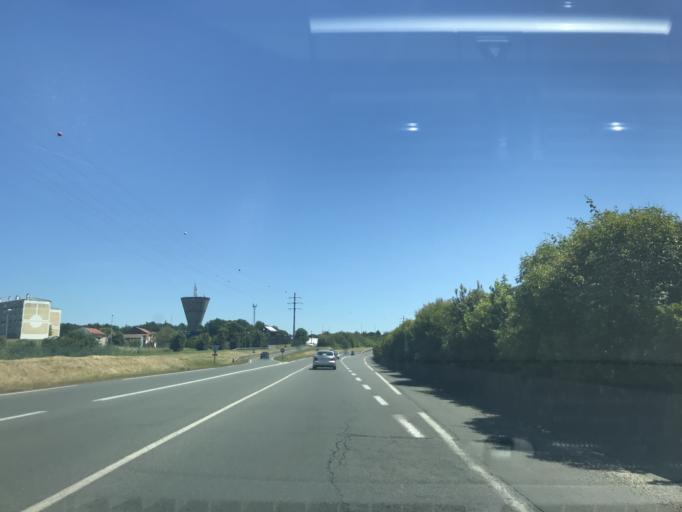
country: FR
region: Poitou-Charentes
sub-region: Departement de la Charente-Maritime
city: Royan
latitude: 45.6287
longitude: -1.0029
